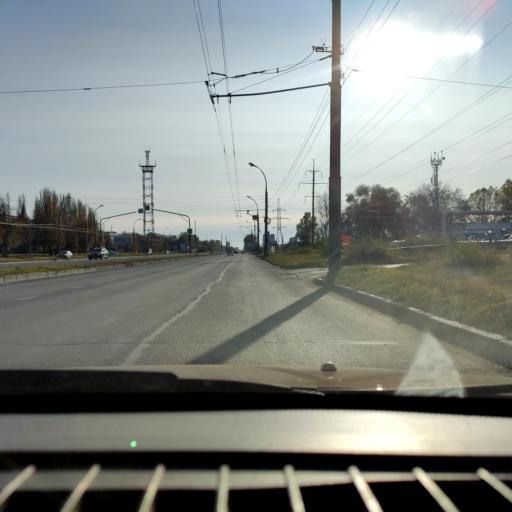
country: RU
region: Samara
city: Tol'yatti
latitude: 53.5337
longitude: 49.2620
